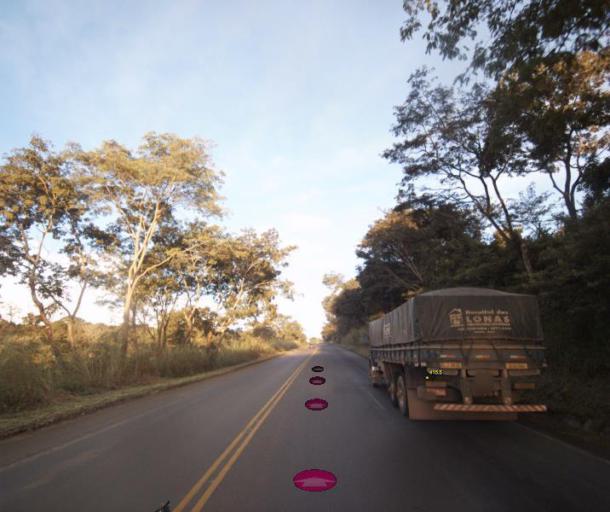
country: BR
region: Goias
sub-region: Abadiania
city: Abadiania
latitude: -16.1026
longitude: -48.8630
